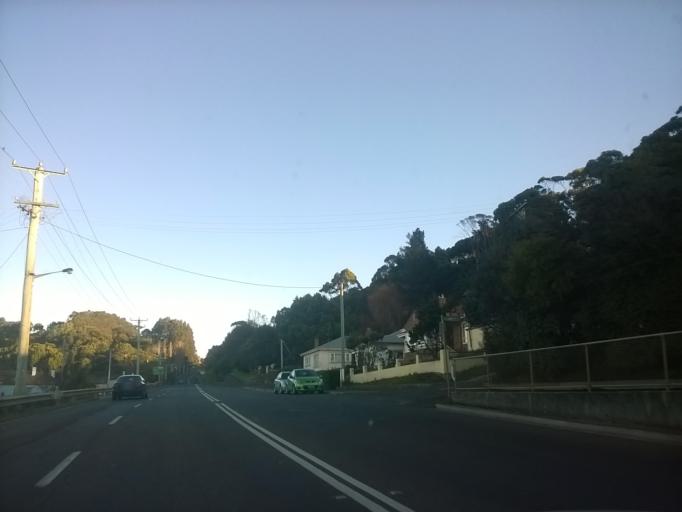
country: AU
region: Tasmania
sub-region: Burnie
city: Burnie
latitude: -41.0567
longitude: 145.9041
